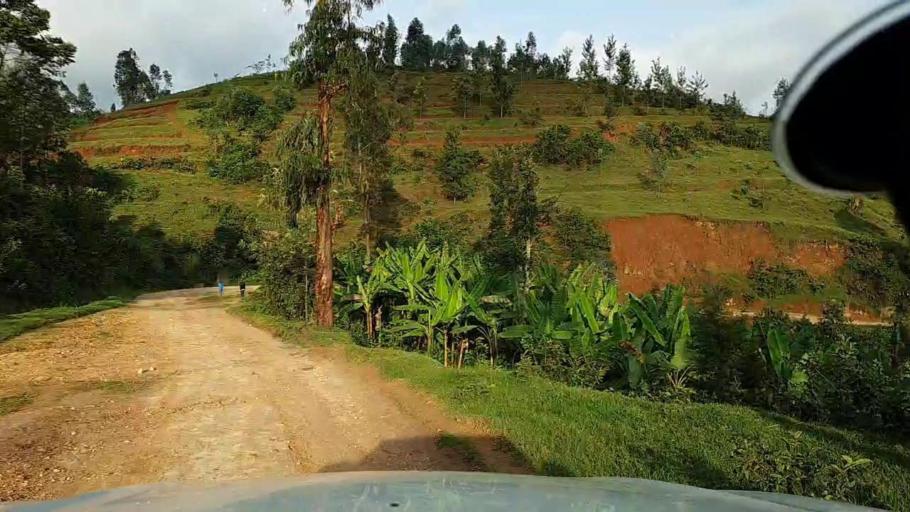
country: RW
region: Southern Province
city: Gitarama
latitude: -2.1906
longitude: 29.5774
